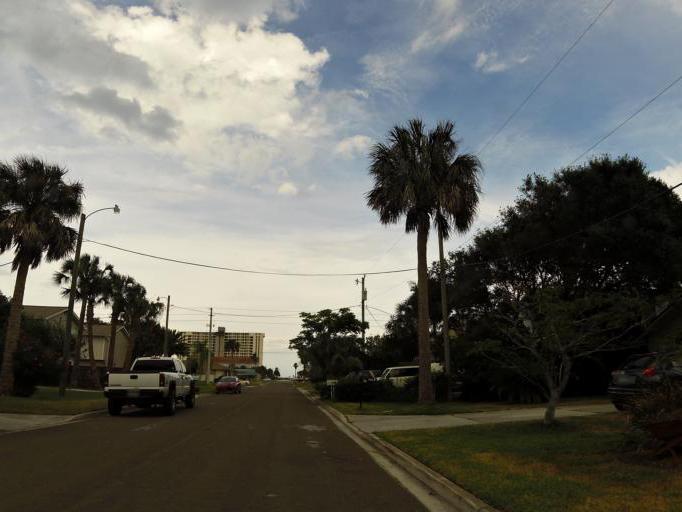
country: US
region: Florida
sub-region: Duval County
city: Jacksonville Beach
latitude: 30.2748
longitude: -81.3911
